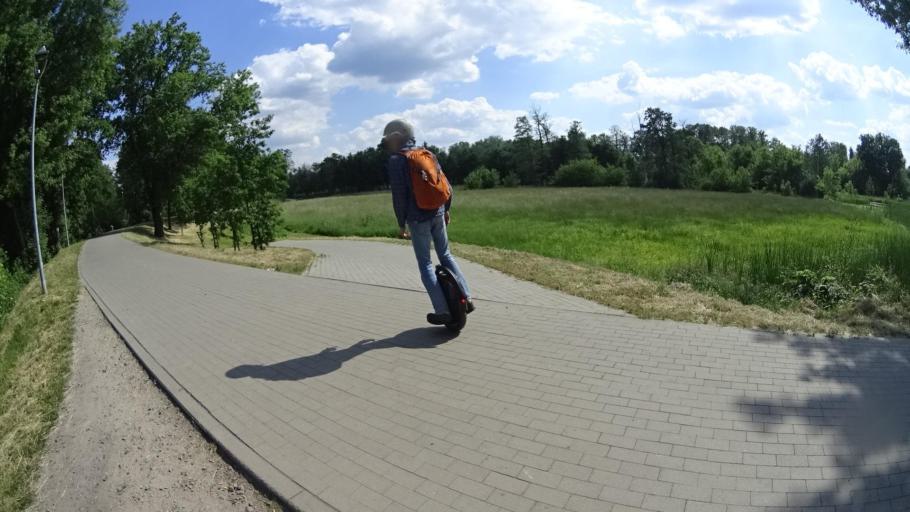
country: PL
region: Masovian Voivodeship
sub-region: Powiat piaseczynski
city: Konstancin-Jeziorna
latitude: 52.0888
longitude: 21.1093
